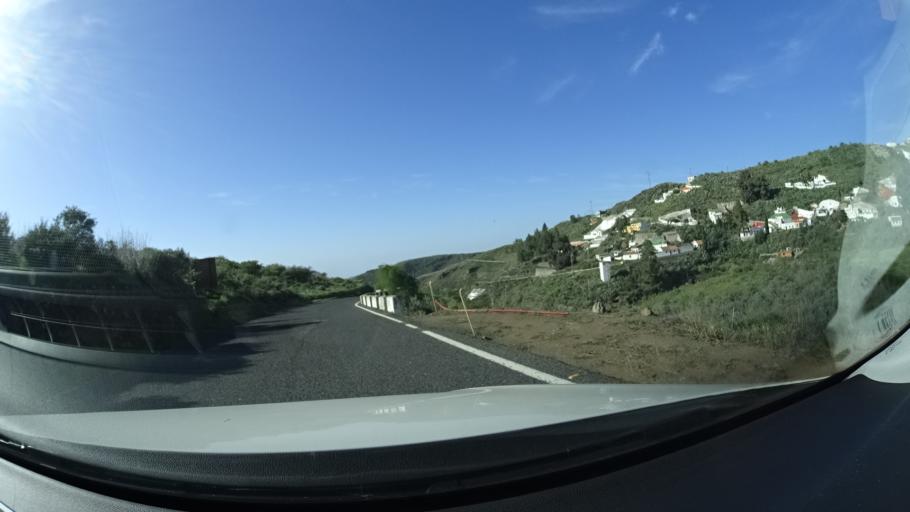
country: ES
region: Canary Islands
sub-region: Provincia de Las Palmas
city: Artenara
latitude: 28.0373
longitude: -15.6424
